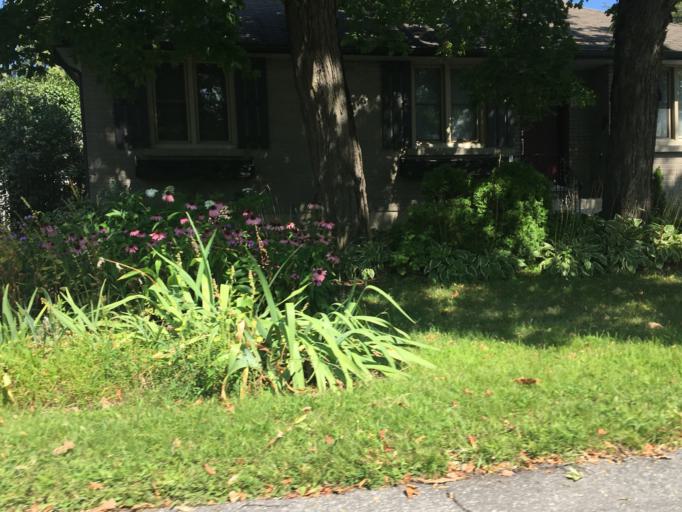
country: CA
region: Ontario
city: Ottawa
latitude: 45.3869
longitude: -75.6598
